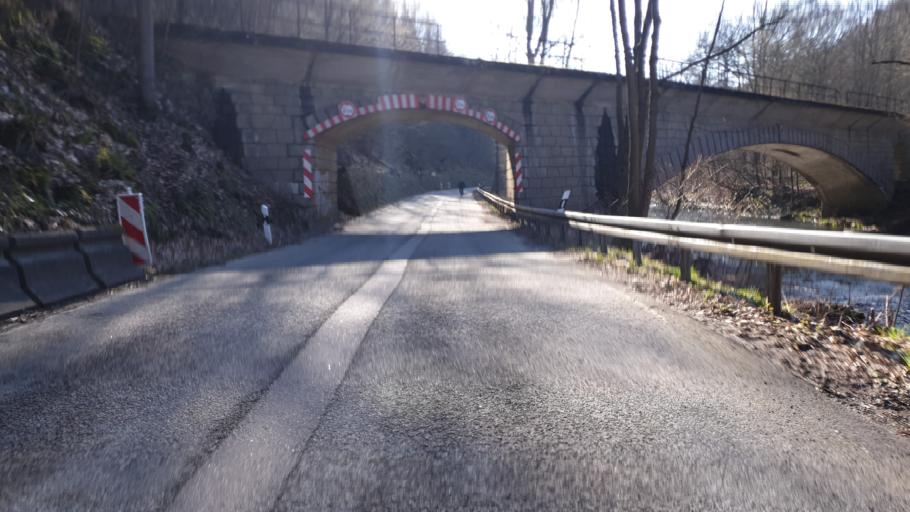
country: DE
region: Saxony
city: Taura
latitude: 50.9422
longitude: 12.8376
